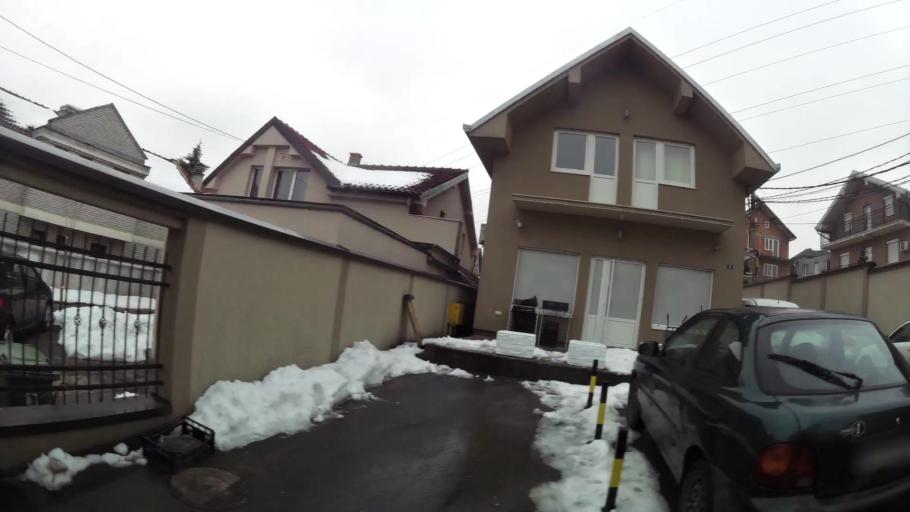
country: RS
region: Central Serbia
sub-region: Belgrade
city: Zvezdara
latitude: 44.7692
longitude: 20.5067
